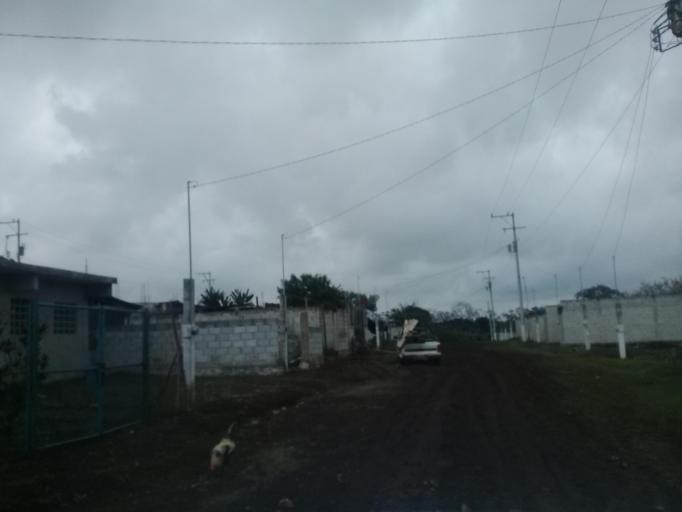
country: MX
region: Veracruz
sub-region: Cordoba
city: San Jose de Tapia
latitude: 18.8500
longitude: -96.9554
